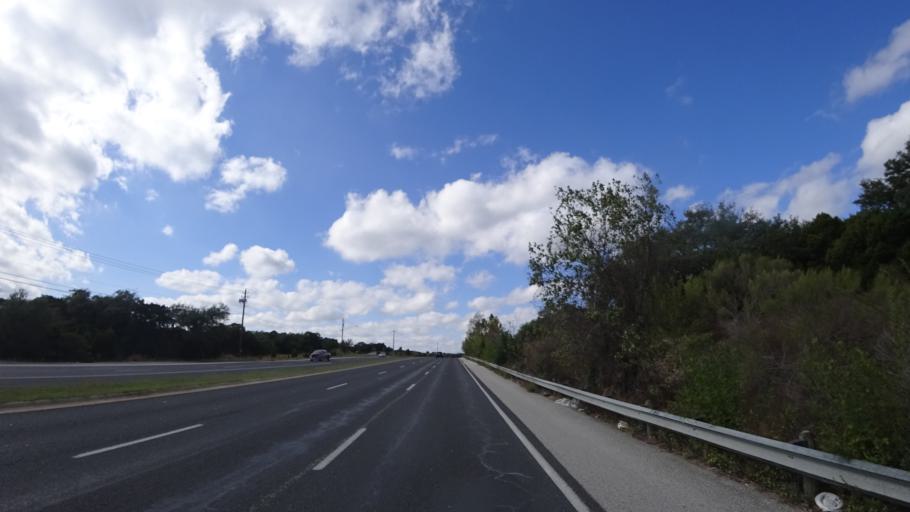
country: US
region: Texas
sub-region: Travis County
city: Barton Creek
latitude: 30.2569
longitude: -97.8772
